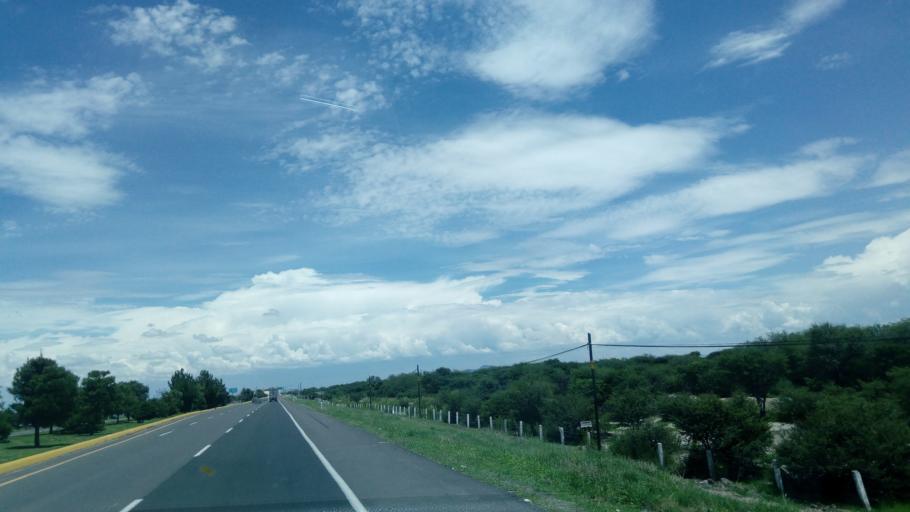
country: MX
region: Durango
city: Victoria de Durango
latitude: 24.1057
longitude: -104.5598
